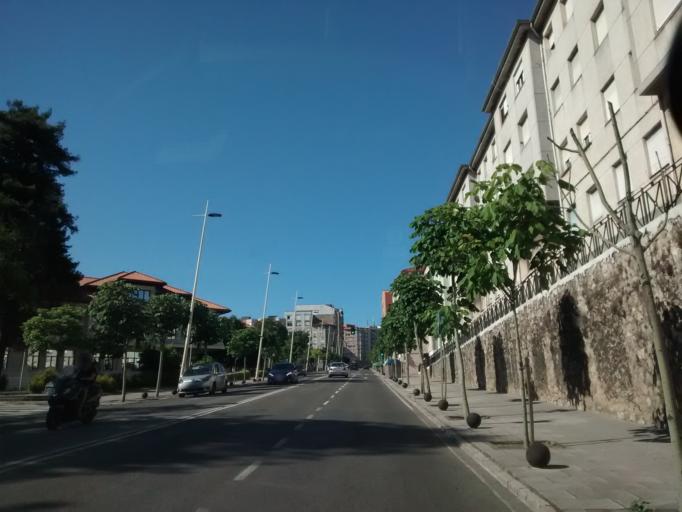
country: ES
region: Cantabria
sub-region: Provincia de Cantabria
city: Santander
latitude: 43.4548
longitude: -3.8275
